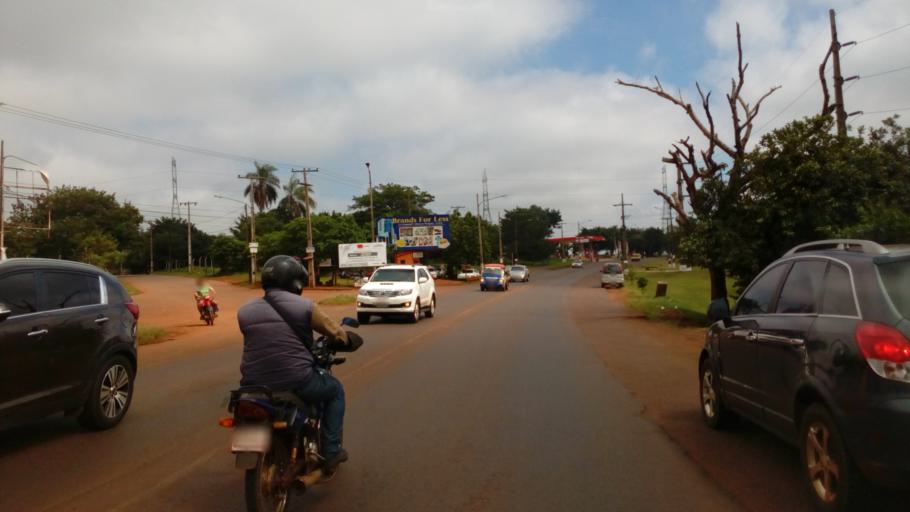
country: PY
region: Alto Parana
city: Ciudad del Este
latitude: -25.4317
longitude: -54.6388
